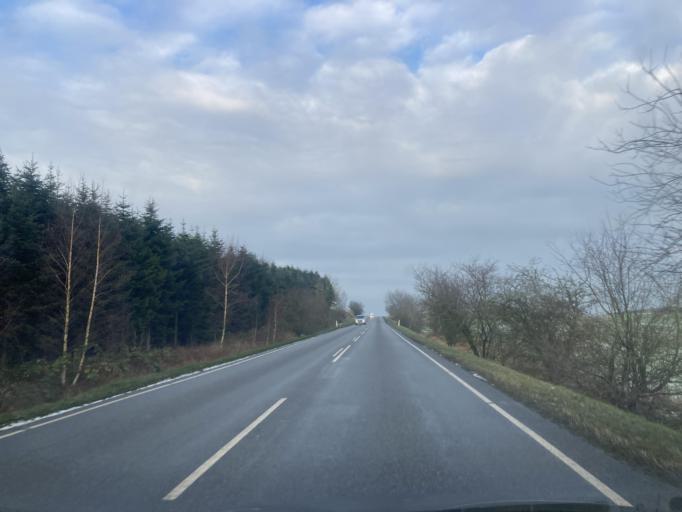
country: DK
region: Zealand
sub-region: Holbaek Kommune
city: Jyderup
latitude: 55.7029
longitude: 11.3867
